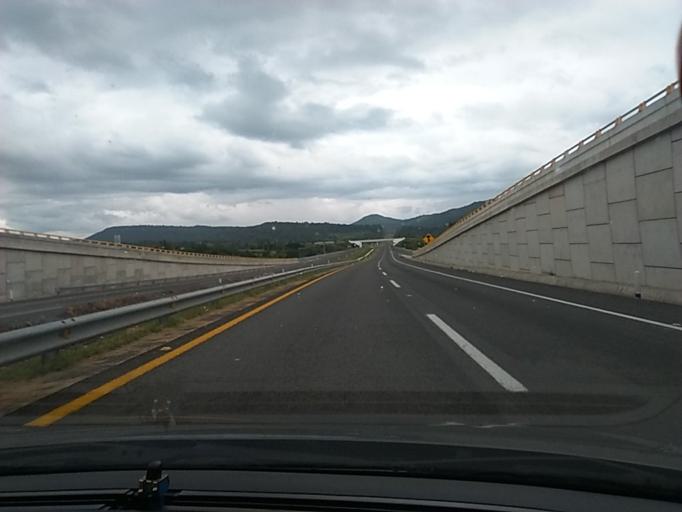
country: MX
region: Jalisco
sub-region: Zapotlanejo
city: La Mezquitera
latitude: 20.5464
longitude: -103.0315
